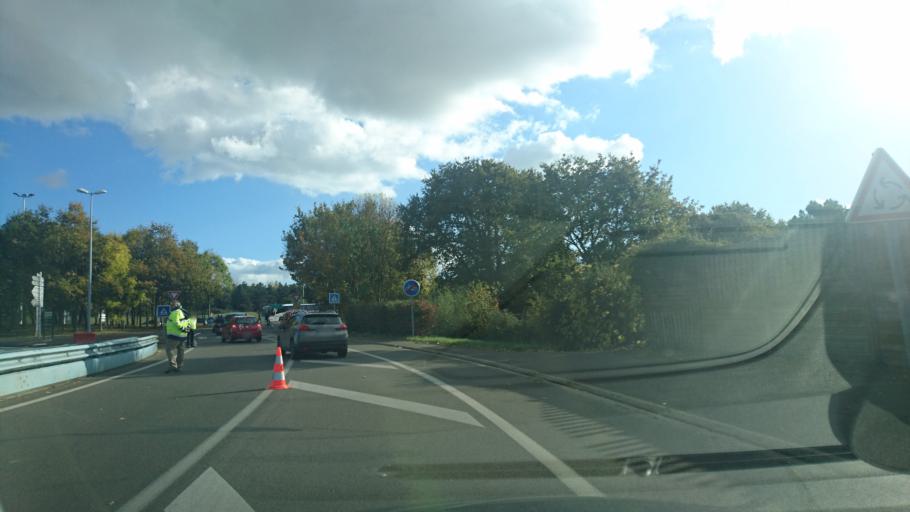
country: FR
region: Pays de la Loire
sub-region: Departement de la Vendee
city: Chateau-d'Olonne
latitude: 46.5157
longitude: -1.7597
